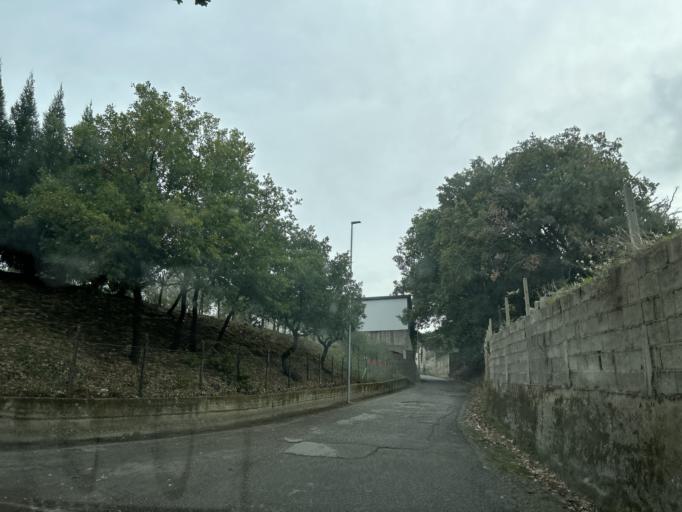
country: IT
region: Calabria
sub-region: Provincia di Catanzaro
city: Staletti
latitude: 38.7667
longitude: 16.5358
